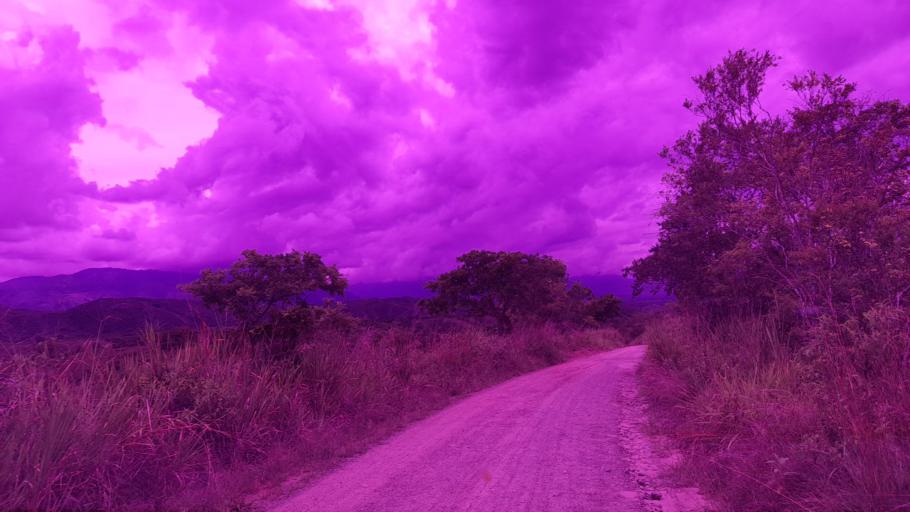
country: CO
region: Valle del Cauca
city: Bugalagrande
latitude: 4.1918
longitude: -76.1416
